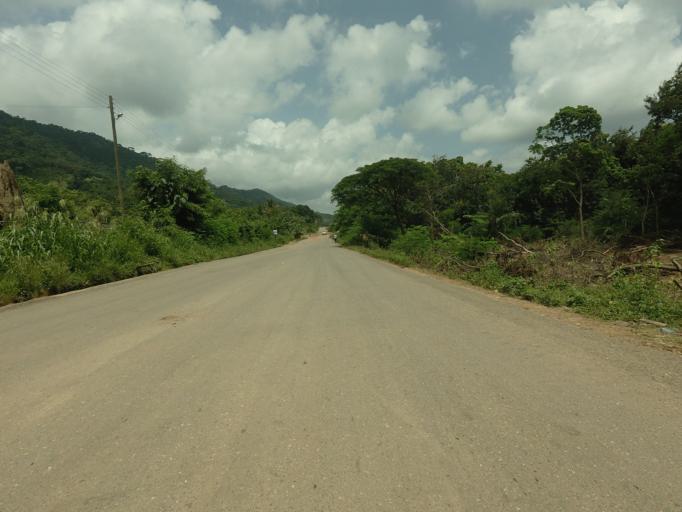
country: GH
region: Volta
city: Ho
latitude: 6.7366
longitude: 0.3479
